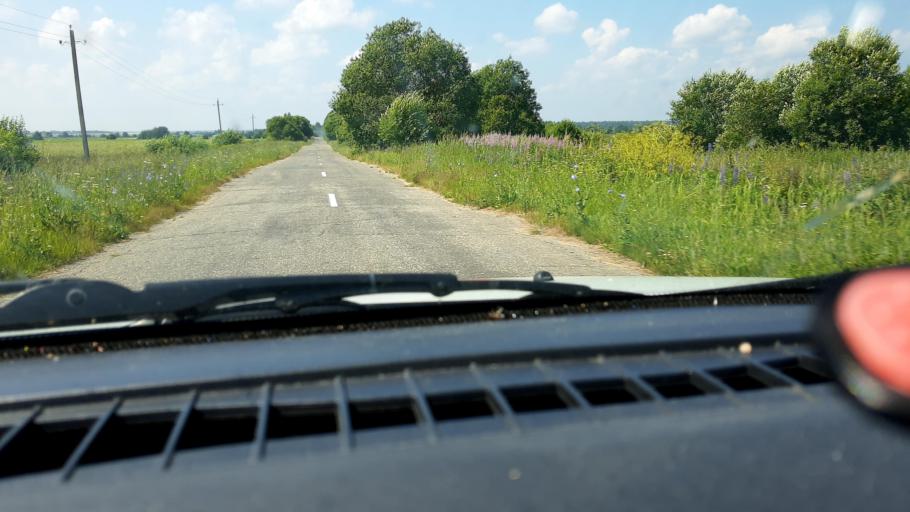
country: RU
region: Nizjnij Novgorod
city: Sharanga
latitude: 57.0597
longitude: 46.6105
